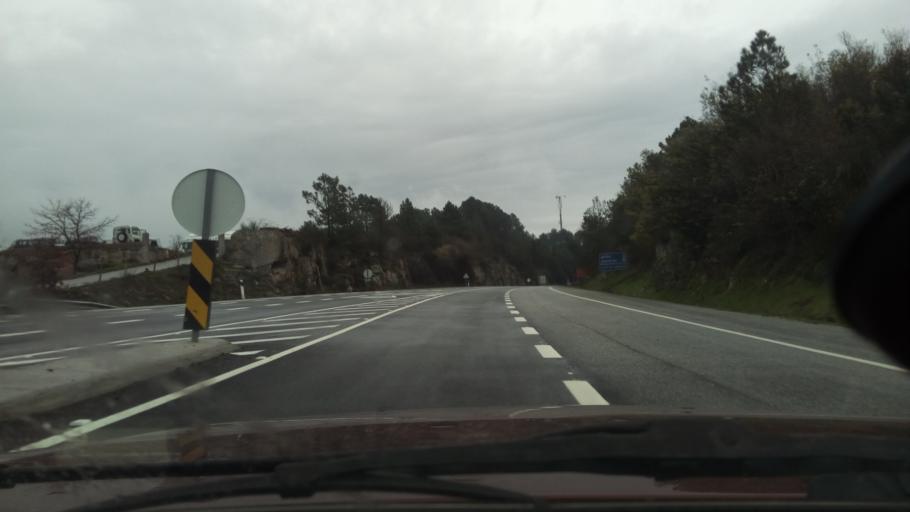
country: PT
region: Guarda
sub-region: Fornos de Algodres
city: Fornos de Algodres
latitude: 40.6178
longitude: -7.6143
